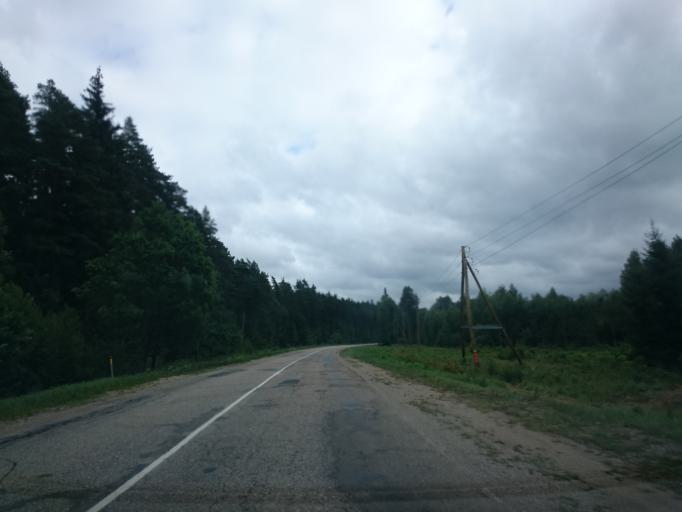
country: LV
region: Pavilostas
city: Pavilosta
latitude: 56.7920
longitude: 21.2431
